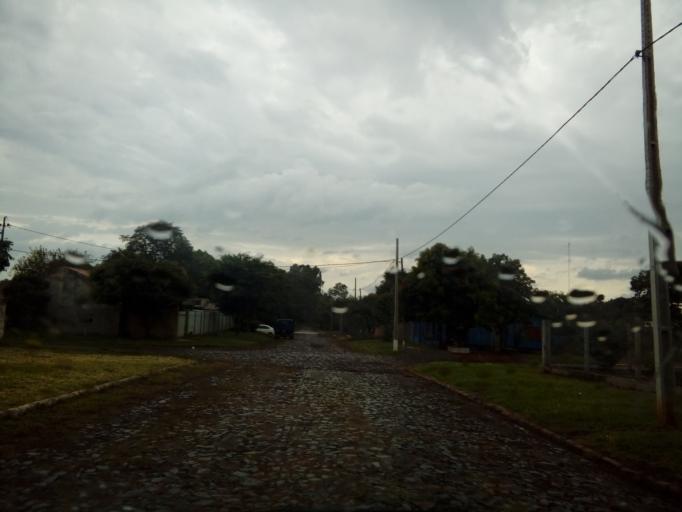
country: PY
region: Alto Parana
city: Ciudad del Este
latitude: -25.4151
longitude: -54.6557
